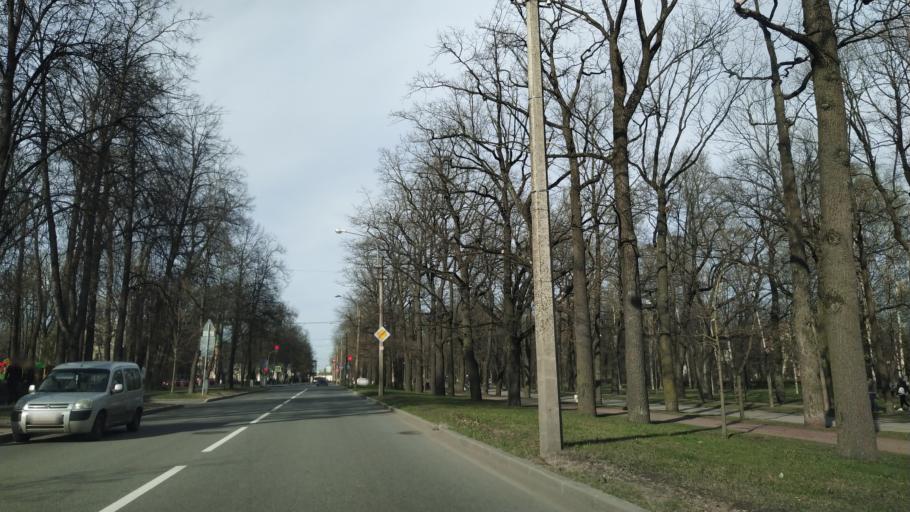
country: RU
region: St.-Petersburg
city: Pushkin
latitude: 59.7186
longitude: 30.4229
